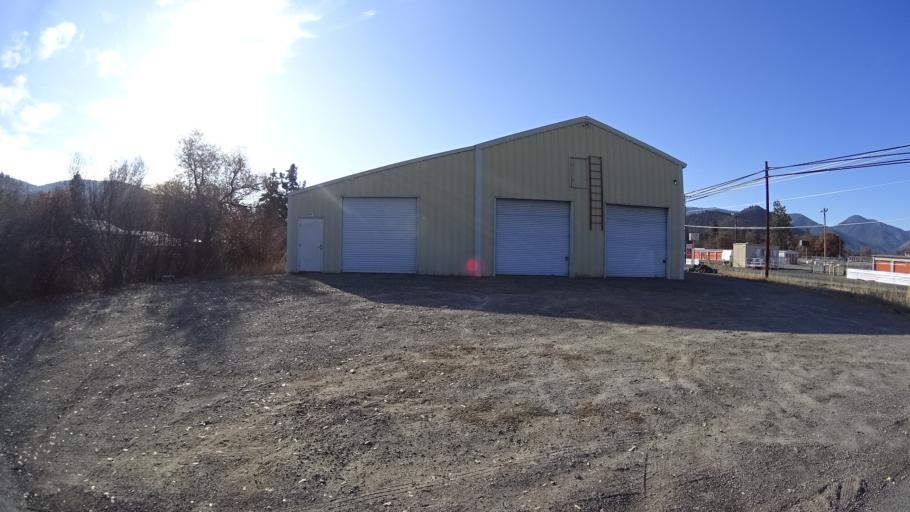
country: US
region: California
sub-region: Siskiyou County
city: Yreka
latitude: 41.6980
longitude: -122.6388
